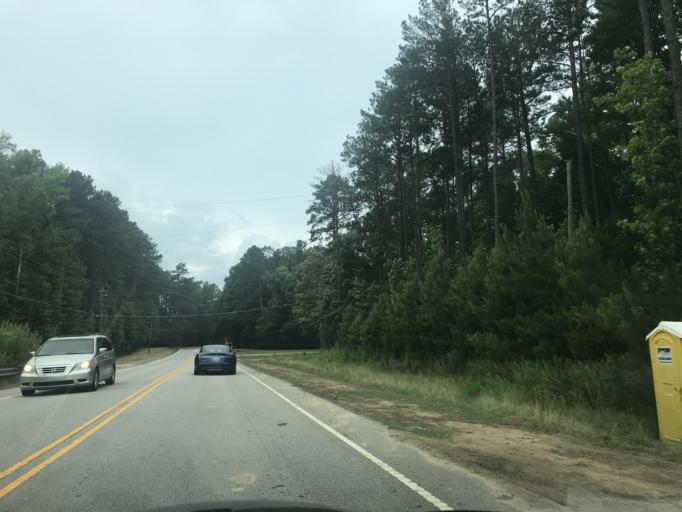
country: US
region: North Carolina
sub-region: Wake County
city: Green Level
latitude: 35.8024
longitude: -78.8921
